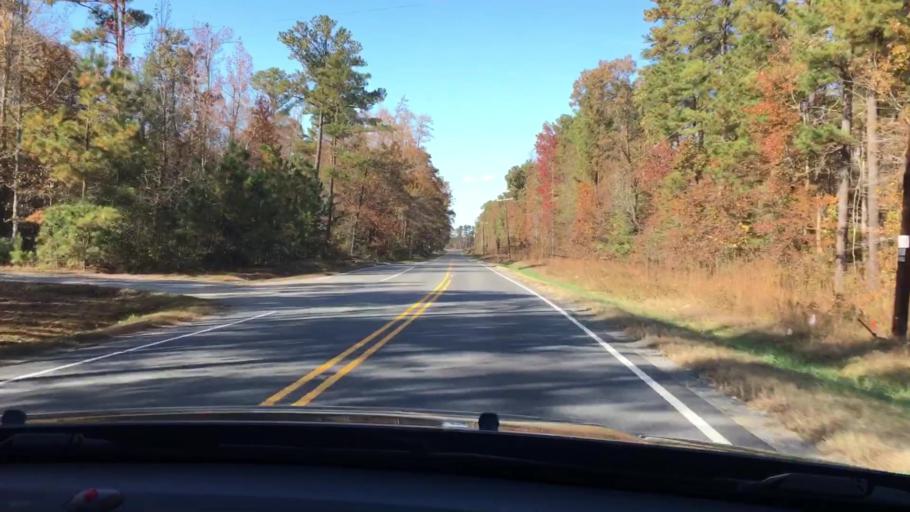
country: US
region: Virginia
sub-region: King and Queen County
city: King and Queen Court House
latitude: 37.6505
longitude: -76.9433
